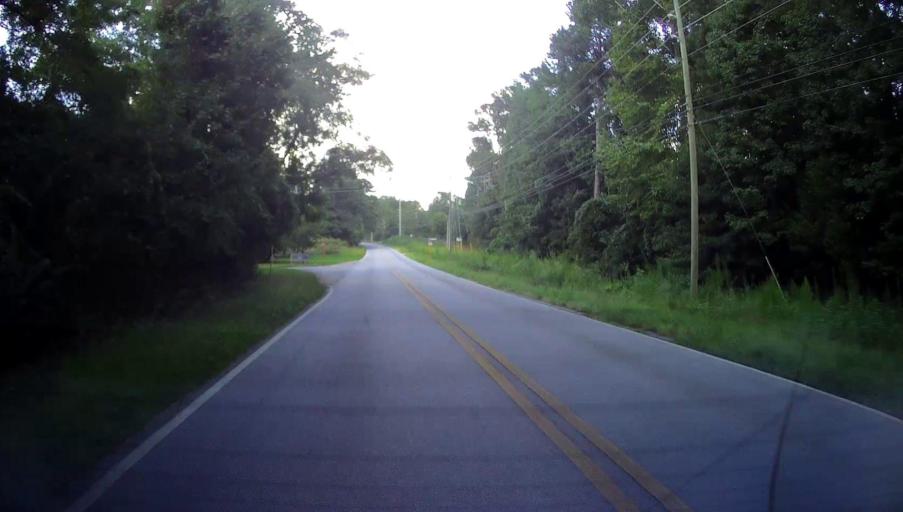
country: US
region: Georgia
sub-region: Muscogee County
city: Columbus
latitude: 32.5386
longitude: -84.9007
